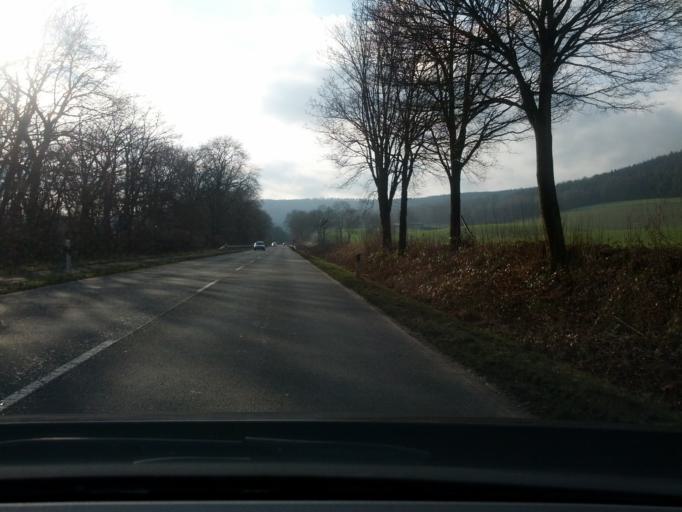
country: DE
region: Lower Saxony
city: Hannoversch Munden
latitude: 51.4458
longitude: 9.6385
